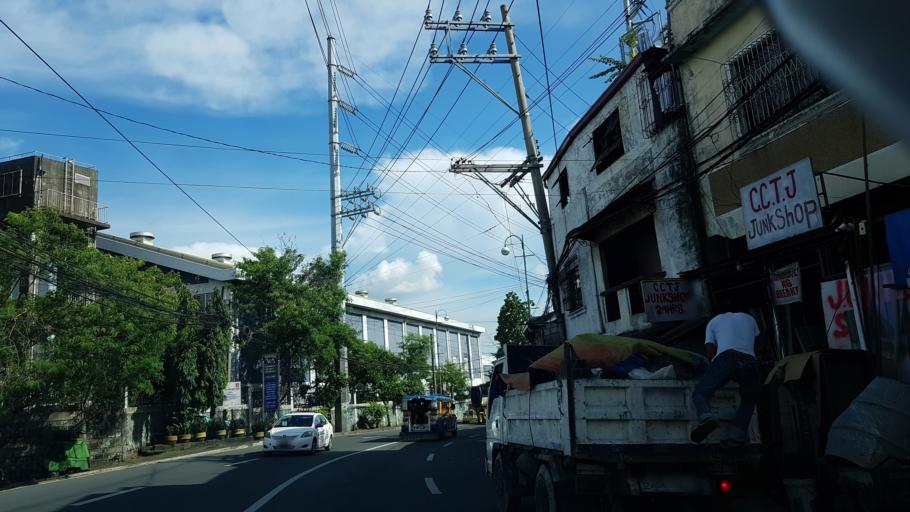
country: PH
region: Calabarzon
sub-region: Province of Rizal
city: Pateros
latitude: 14.5588
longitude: 121.0661
